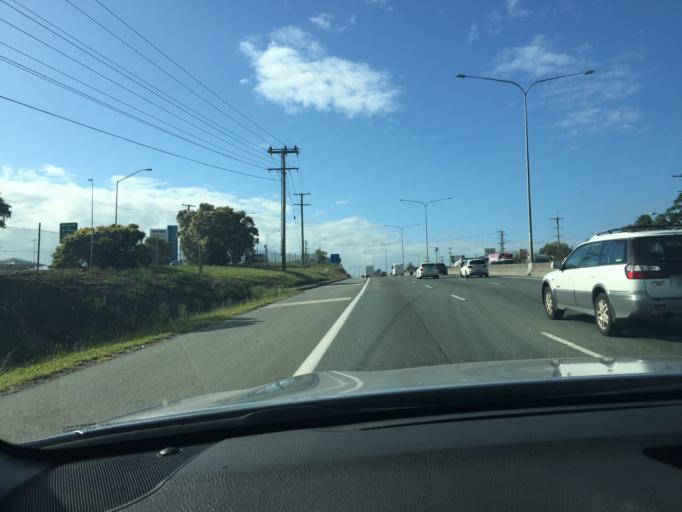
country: AU
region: Queensland
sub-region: Logan
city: Slacks Creek
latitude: -27.6604
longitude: 153.1690
